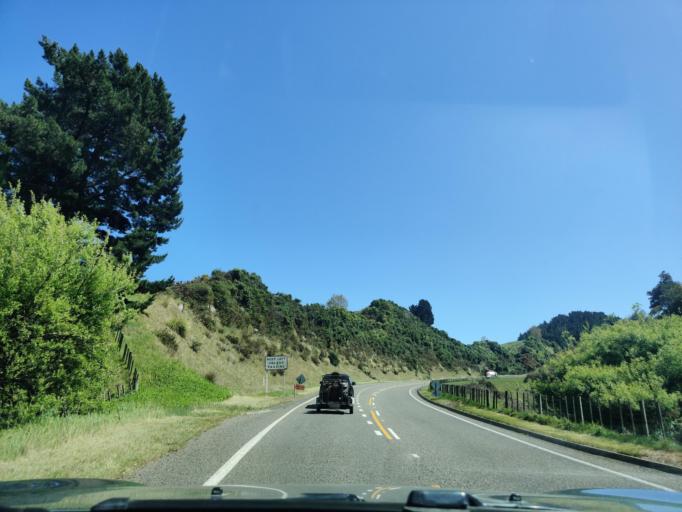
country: NZ
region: Manawatu-Wanganui
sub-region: Wanganui District
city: Wanganui
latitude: -39.8315
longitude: 174.8857
